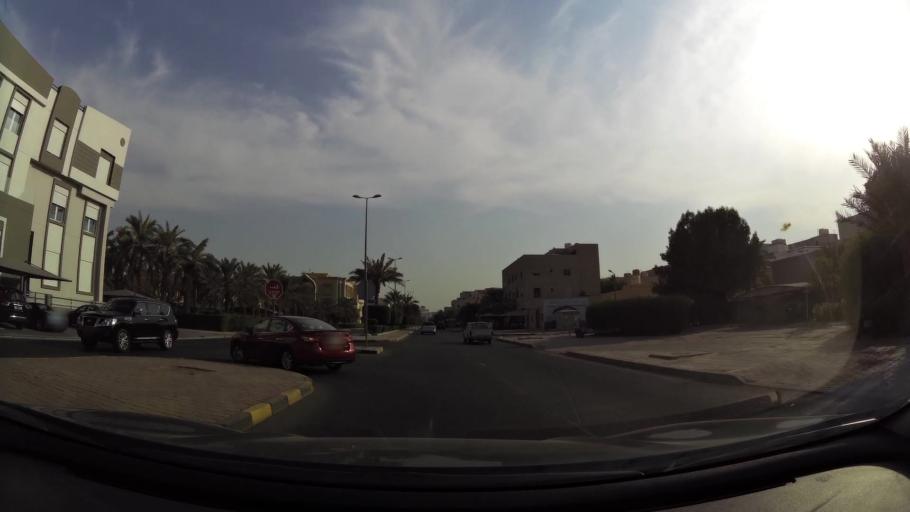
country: KW
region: Muhafazat Hawalli
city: Hawalli
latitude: 29.3255
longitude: 48.0023
